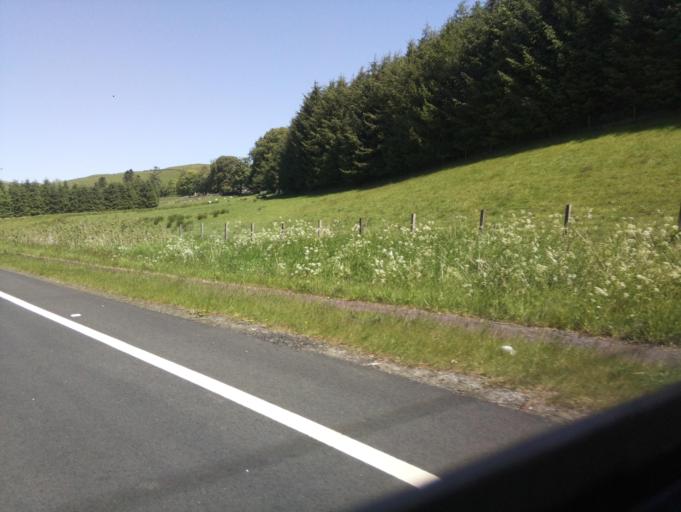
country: GB
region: Scotland
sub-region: The Scottish Borders
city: Hawick
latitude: 55.3311
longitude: -2.9418
